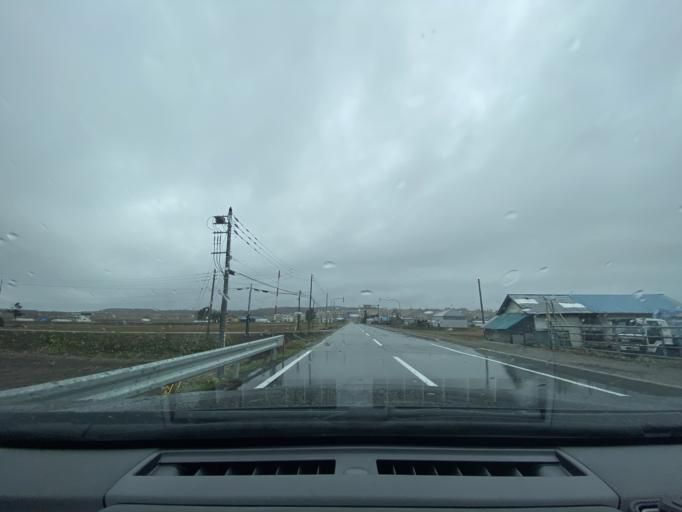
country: JP
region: Hokkaido
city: Fukagawa
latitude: 43.8062
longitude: 141.9091
